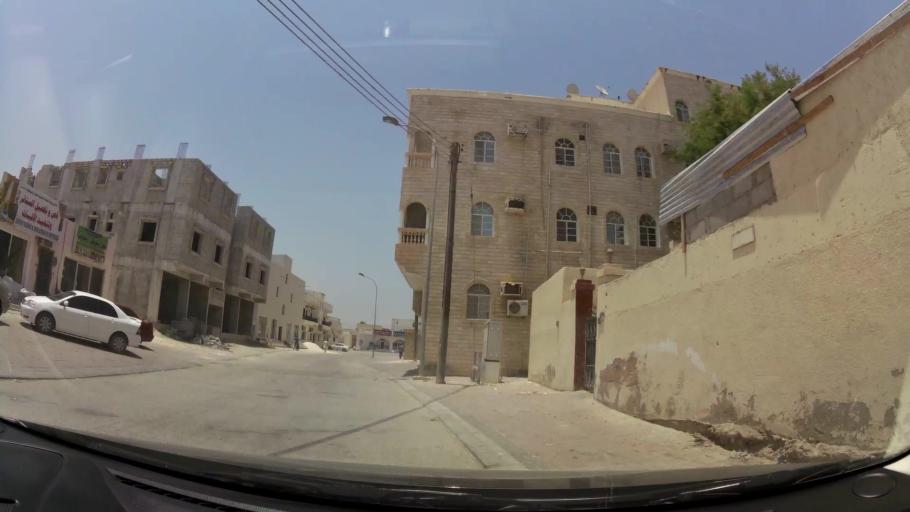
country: OM
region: Zufar
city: Salalah
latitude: 17.0150
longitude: 54.1033
